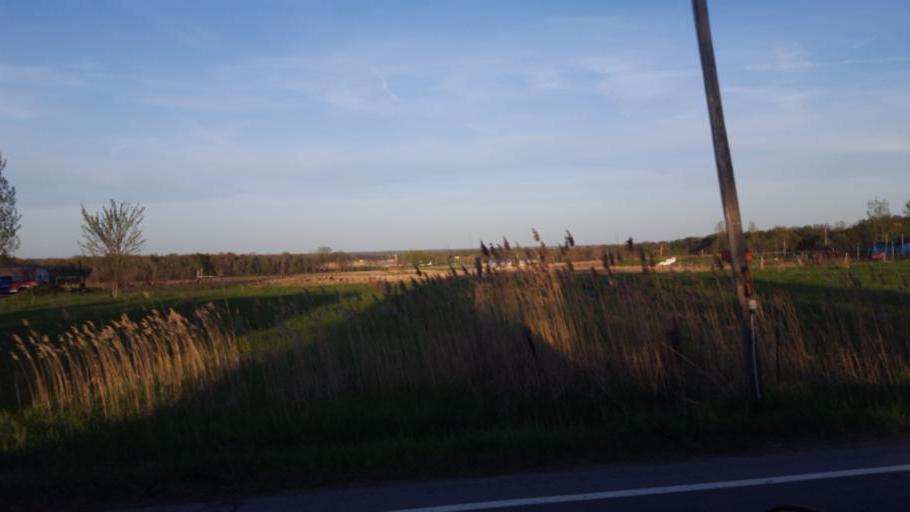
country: US
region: Ohio
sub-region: Ashtabula County
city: Andover
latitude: 41.5482
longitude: -80.5704
